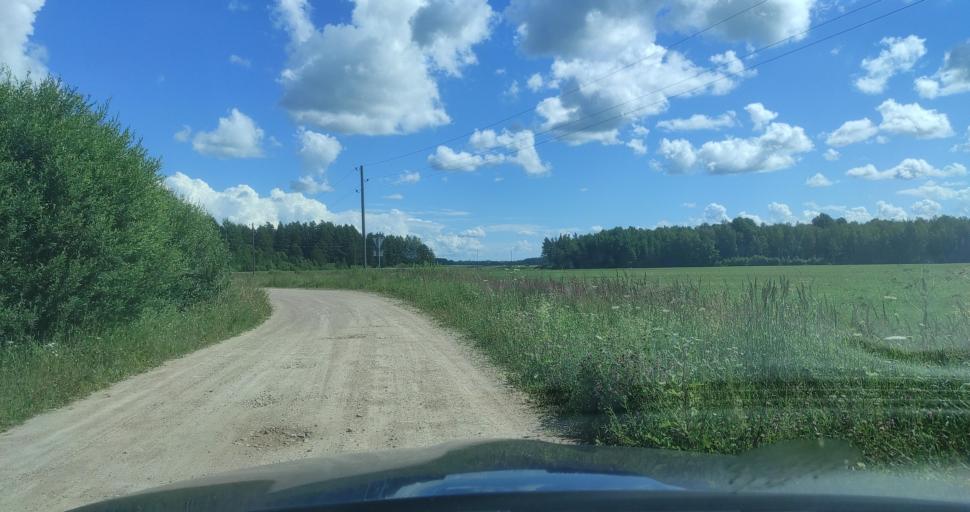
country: LV
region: Kuldigas Rajons
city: Kuldiga
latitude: 56.9935
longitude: 22.1118
